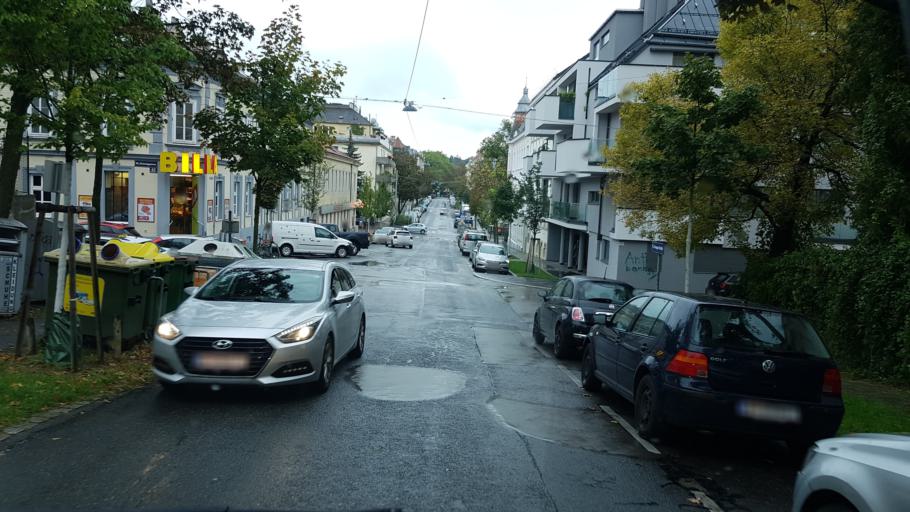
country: AT
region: Vienna
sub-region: Wien Stadt
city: Vienna
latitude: 48.2307
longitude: 16.3241
